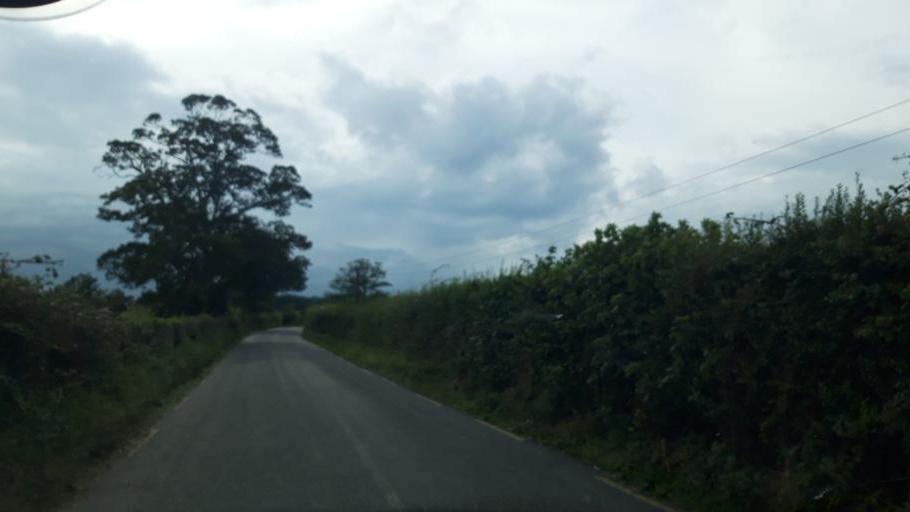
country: IE
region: Leinster
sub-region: Kilkenny
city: Ballyragget
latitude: 52.7574
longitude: -7.3843
